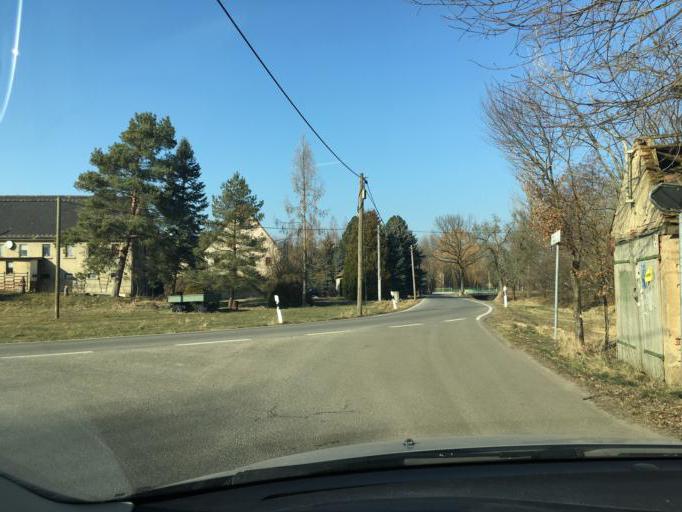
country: DE
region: Thuringia
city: Frohnsdorf
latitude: 50.9078
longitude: 12.5719
